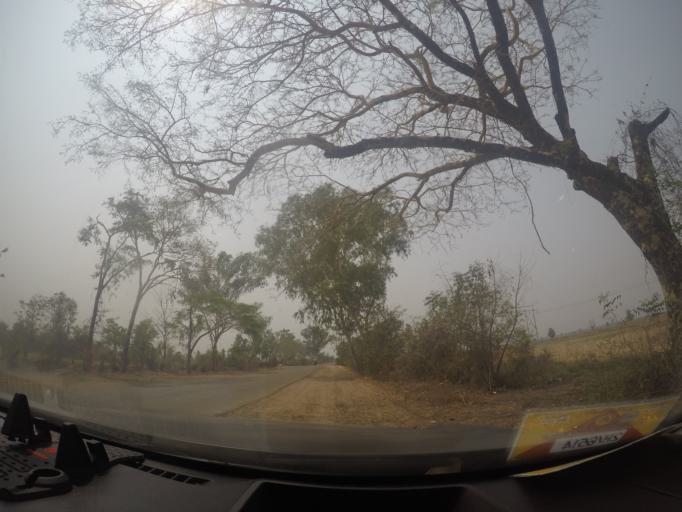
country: MM
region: Magway
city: Taungdwingyi
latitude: 19.8501
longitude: 95.4877
